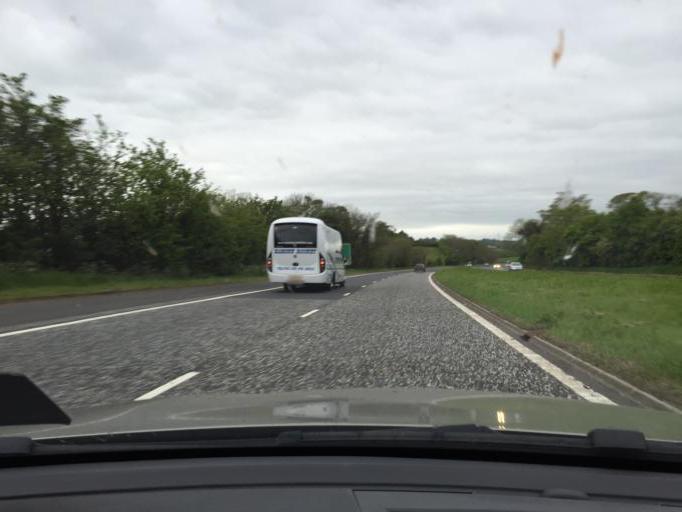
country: GB
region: Northern Ireland
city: Moira
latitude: 54.3918
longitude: -6.1764
